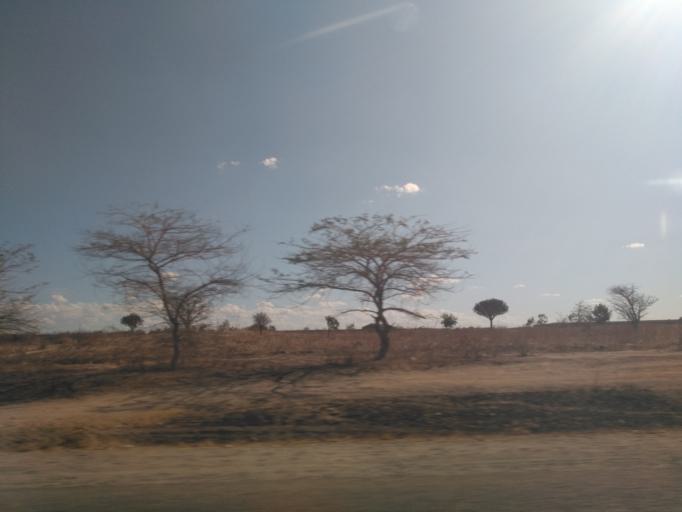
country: TZ
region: Dodoma
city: Dodoma
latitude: -6.1526
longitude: 35.7076
